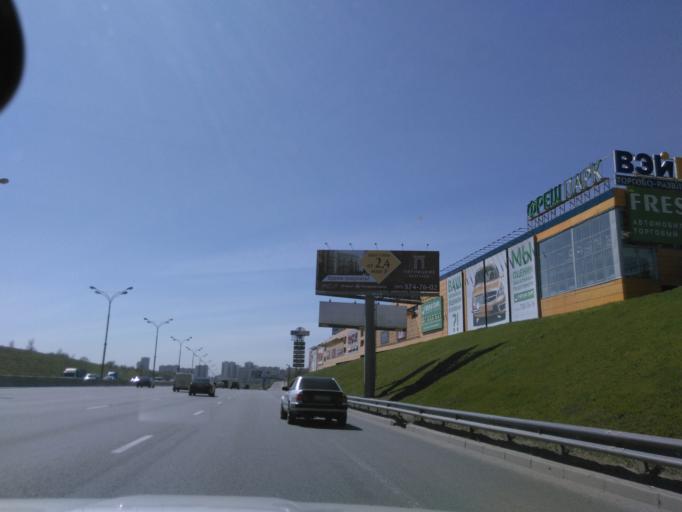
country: RU
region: Moscow
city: Strogino
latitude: 55.8596
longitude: 37.3977
